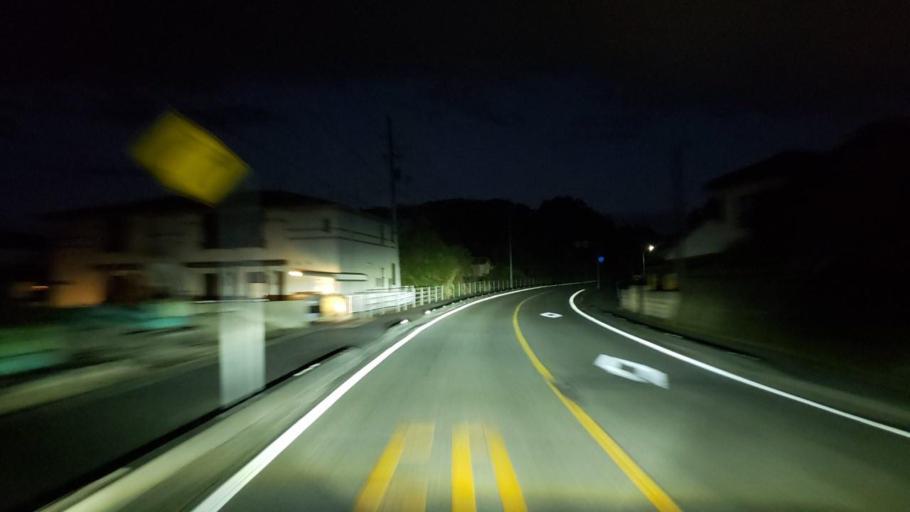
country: JP
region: Tokushima
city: Narutocho-mitsuishi
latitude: 34.2077
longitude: 134.5775
